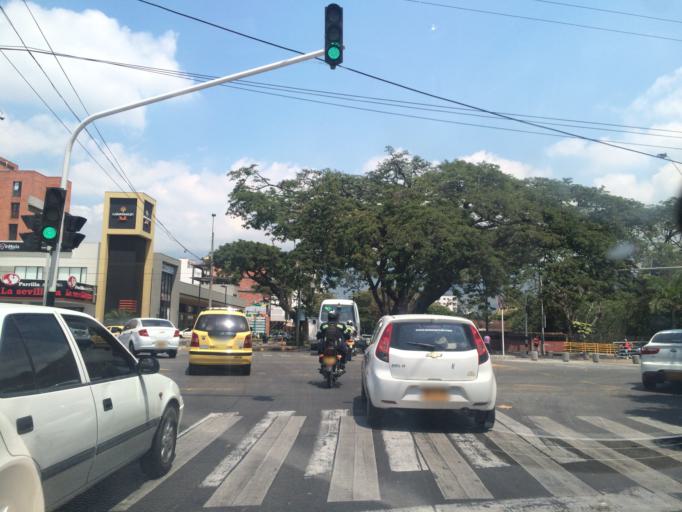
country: CO
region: Valle del Cauca
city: Cali
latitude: 3.4089
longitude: -76.5470
